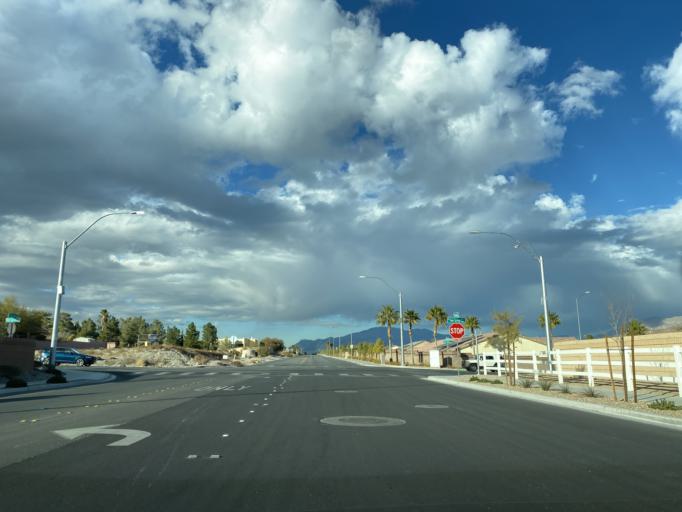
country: US
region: Nevada
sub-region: Clark County
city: Summerlin South
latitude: 36.2841
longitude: -115.3059
